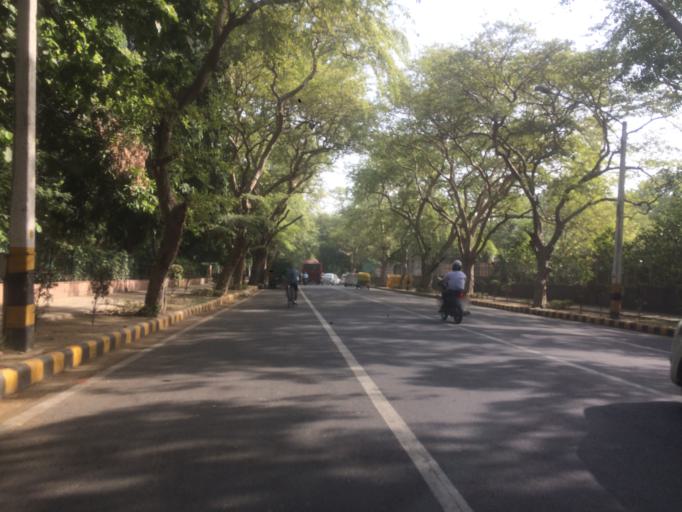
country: IN
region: NCT
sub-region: New Delhi
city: New Delhi
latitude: 28.6237
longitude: 77.1979
